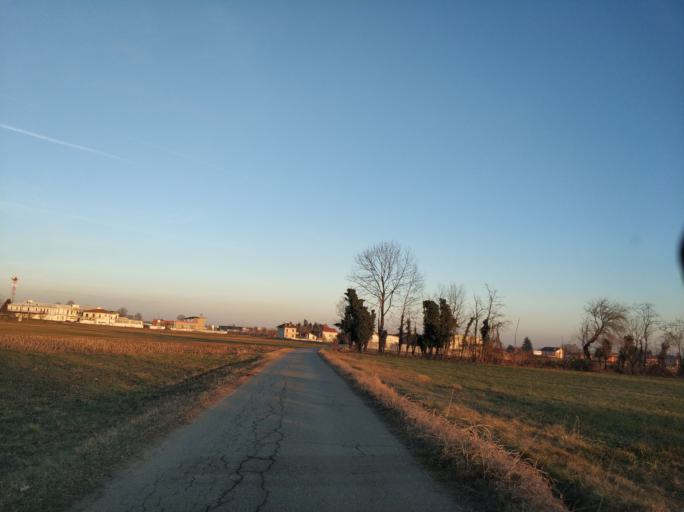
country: IT
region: Piedmont
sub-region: Provincia di Torino
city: Caselle Torinese
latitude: 45.1884
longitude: 7.6311
